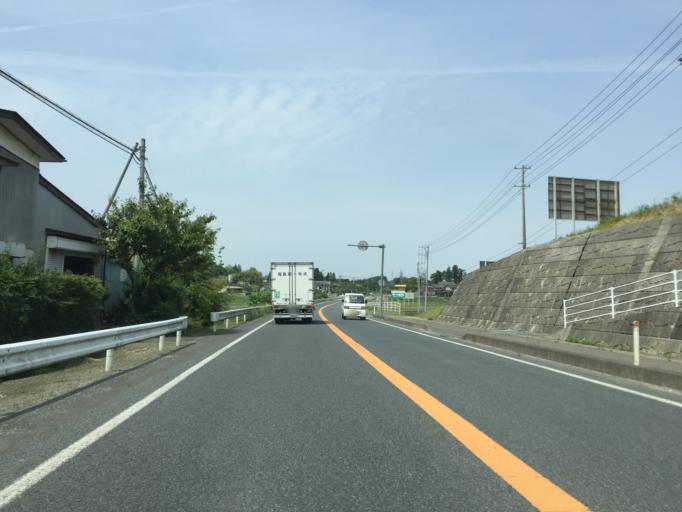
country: JP
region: Miyagi
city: Marumori
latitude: 37.8200
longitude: 140.9207
